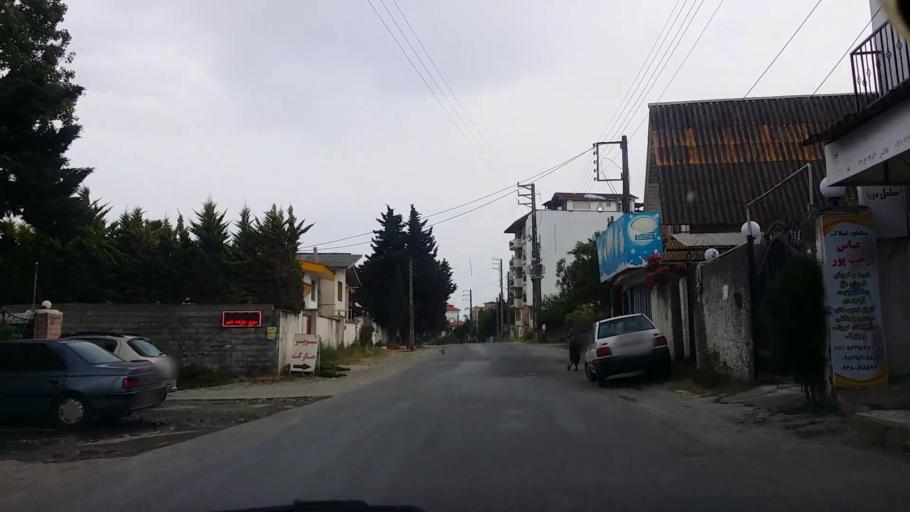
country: IR
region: Mazandaran
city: Chalus
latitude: 36.6862
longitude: 51.4111
